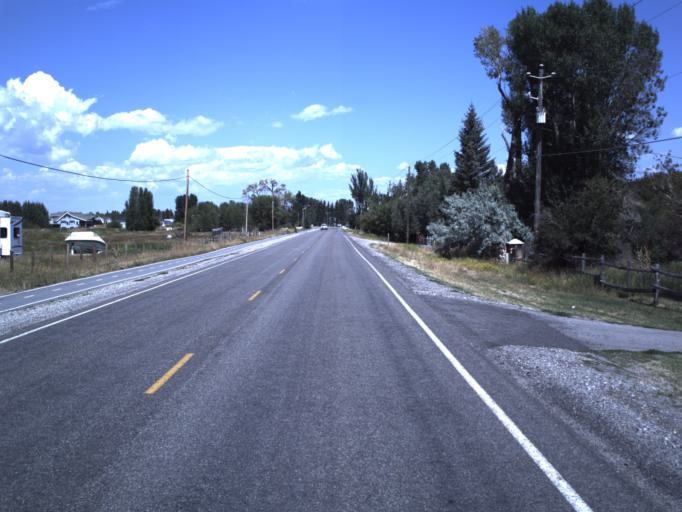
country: US
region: Idaho
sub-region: Bear Lake County
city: Paris
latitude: 41.9311
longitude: -111.3957
